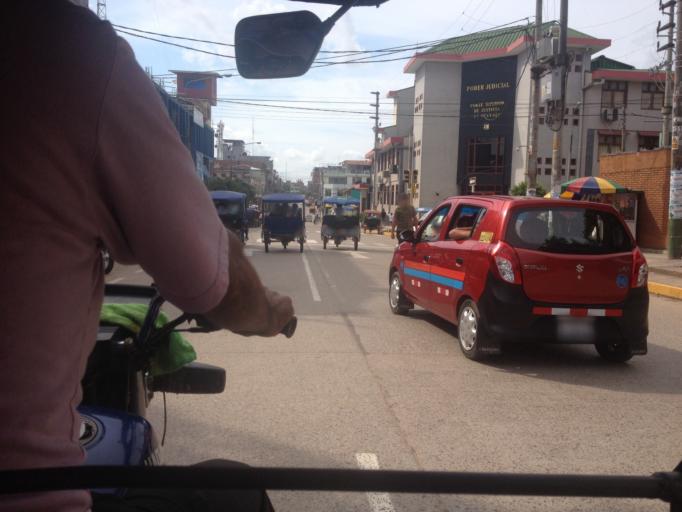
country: PE
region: Ucayali
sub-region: Provincia de Coronel Portillo
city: Pucallpa
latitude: -8.3850
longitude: -74.5324
